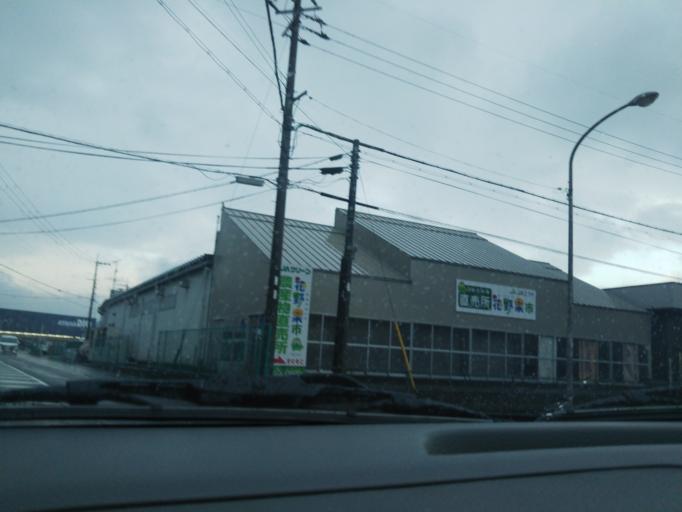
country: JP
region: Shiga Prefecture
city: Minakuchicho-matoba
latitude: 34.9649
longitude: 136.1683
